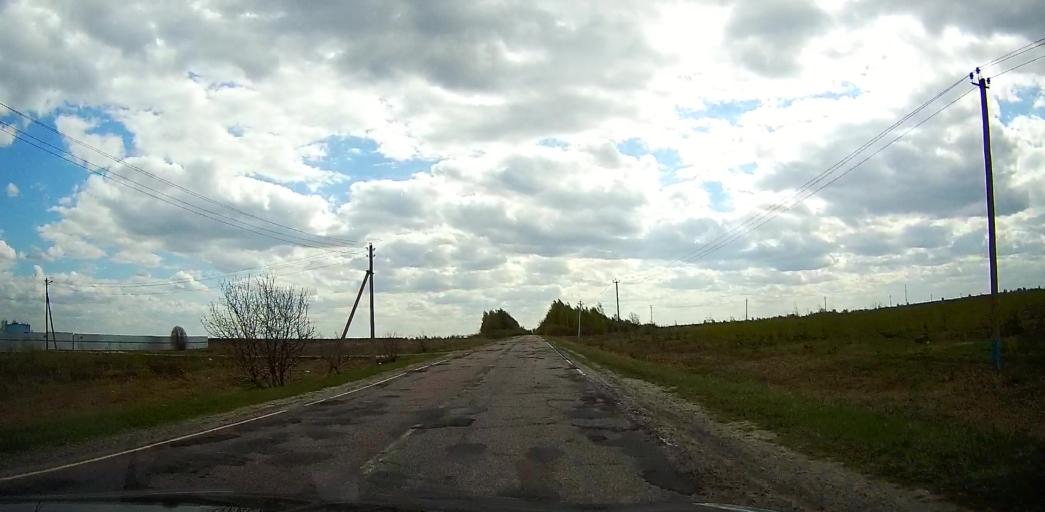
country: RU
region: Moskovskaya
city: Davydovo
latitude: 55.6394
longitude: 38.7484
